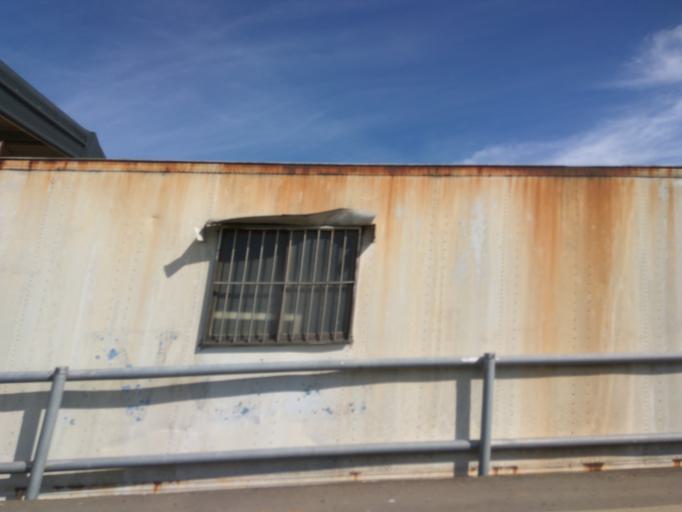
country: TW
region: Taiwan
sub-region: Hsinchu
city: Zhubei
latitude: 25.0155
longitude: 121.0880
